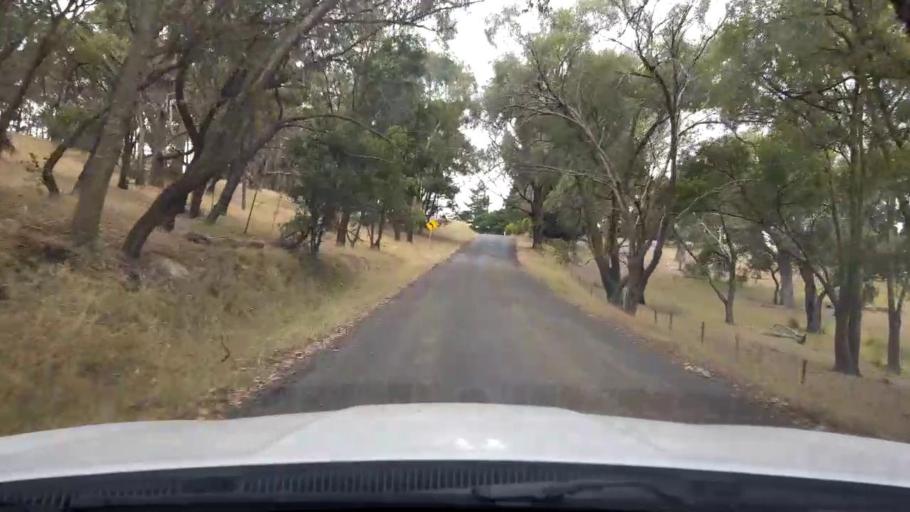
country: AU
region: Victoria
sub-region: Whittlesea
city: Whittlesea
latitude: -37.4914
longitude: 145.0524
